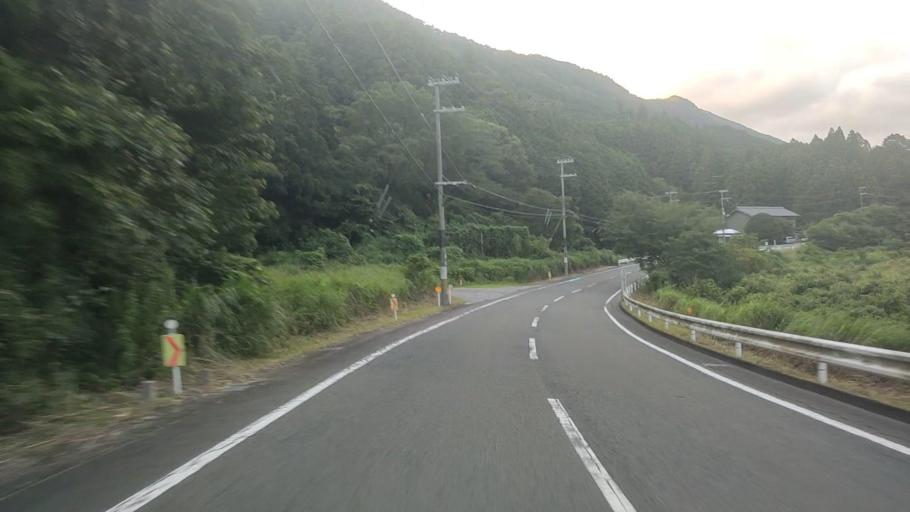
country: JP
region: Wakayama
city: Tanabe
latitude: 33.8245
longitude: 135.6320
